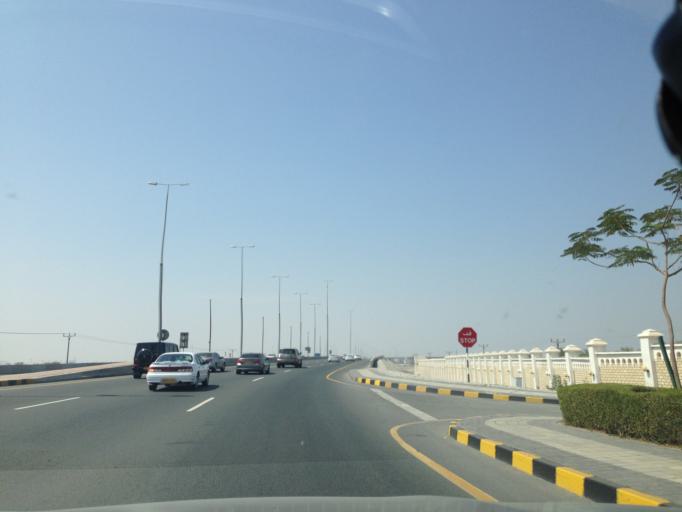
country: OM
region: Muhafazat Masqat
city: As Sib al Jadidah
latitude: 23.6633
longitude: 58.1698
